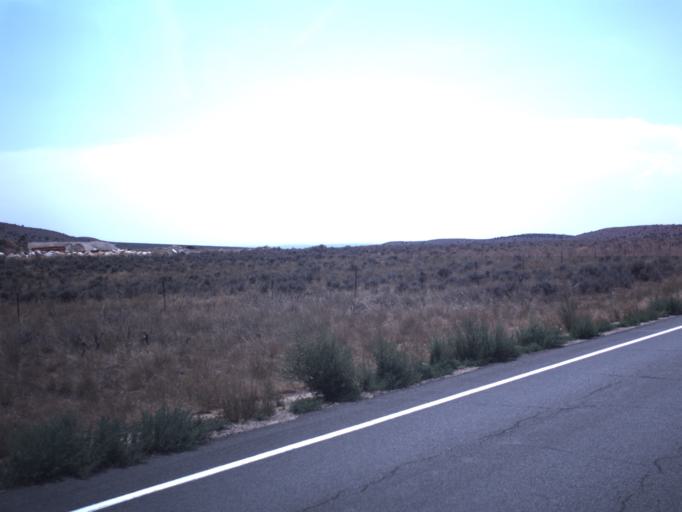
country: US
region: Utah
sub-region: Uintah County
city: Maeser
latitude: 40.4465
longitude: -109.6316
